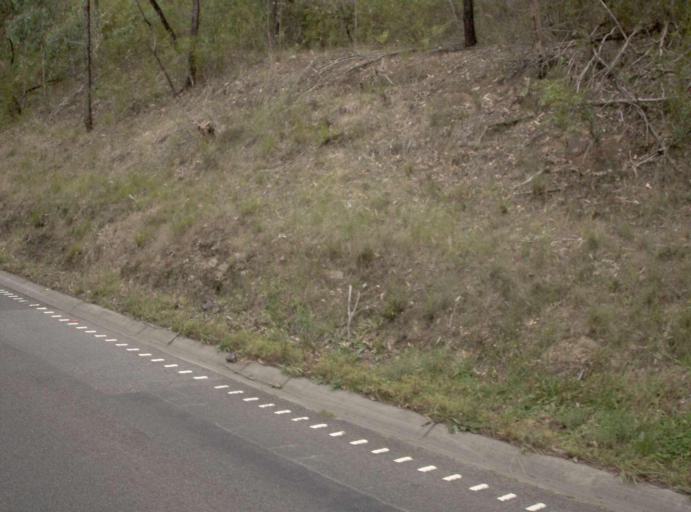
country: AU
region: Victoria
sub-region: Yarra Ranges
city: Yarra Glen
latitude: -37.5430
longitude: 145.4160
